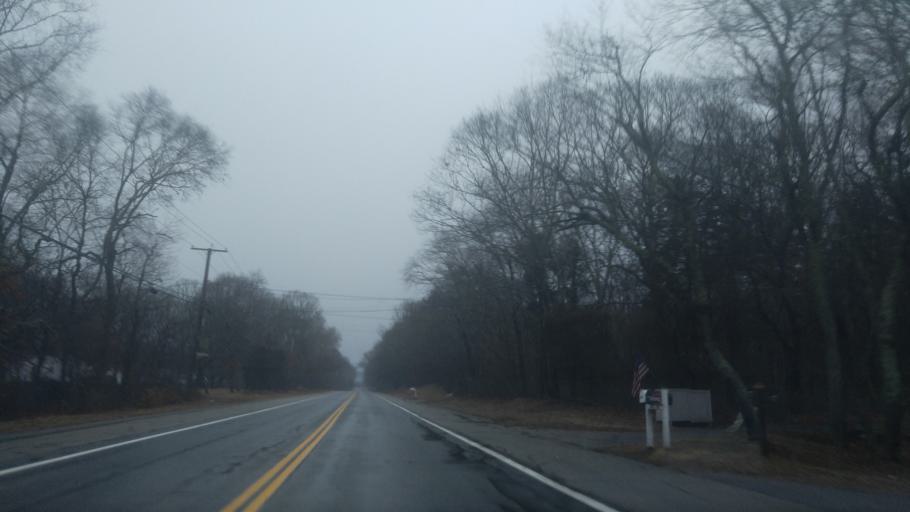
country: US
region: Rhode Island
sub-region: Washington County
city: Kingston
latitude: 41.5001
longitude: -71.5632
